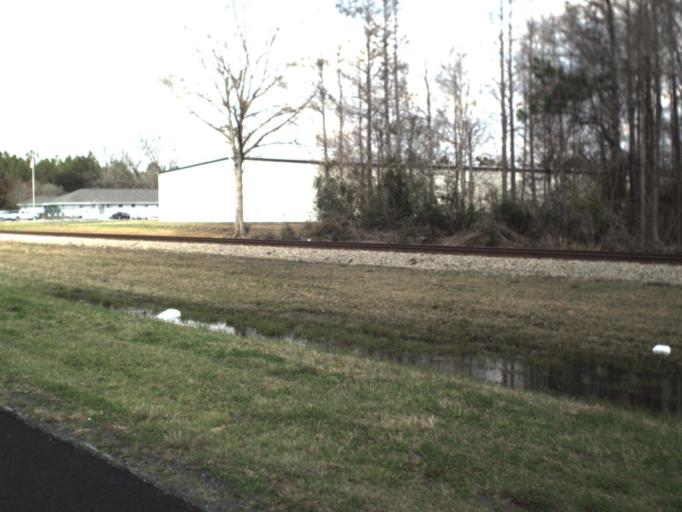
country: US
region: Florida
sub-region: Bay County
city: Youngstown
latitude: 30.3449
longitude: -85.4407
